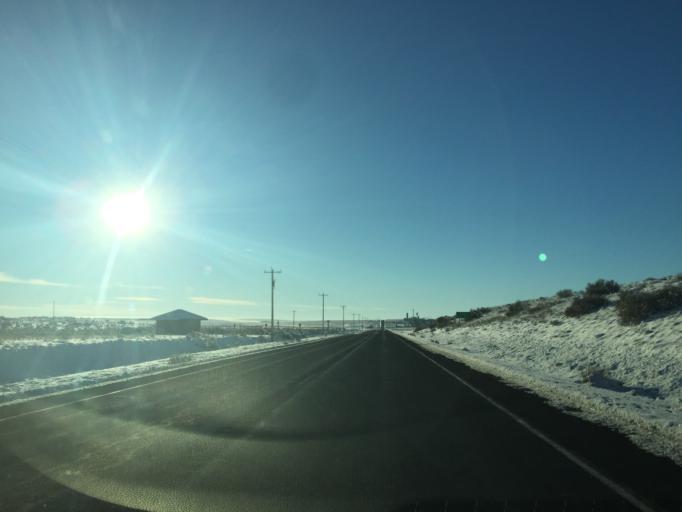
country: US
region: Washington
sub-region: Okanogan County
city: Coulee Dam
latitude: 47.7150
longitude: -118.9131
